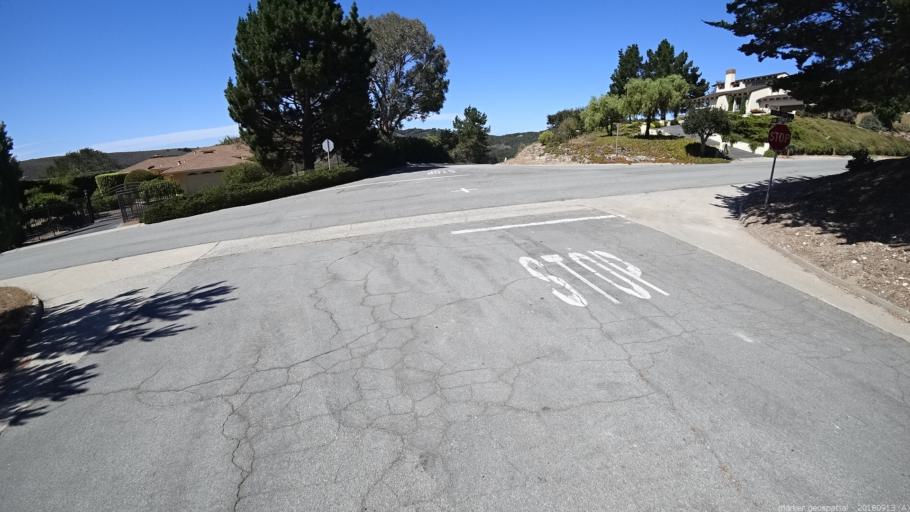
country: US
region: California
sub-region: Monterey County
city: Carmel Valley Village
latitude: 36.5413
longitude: -121.7969
